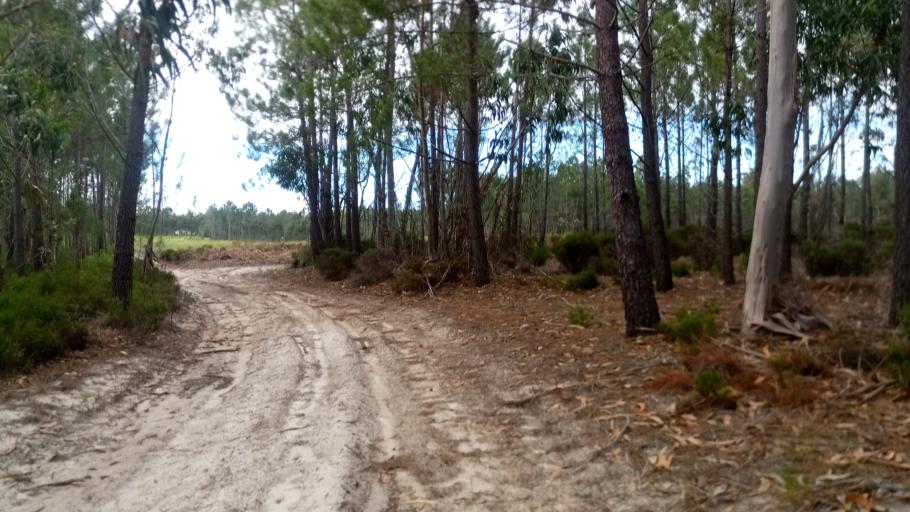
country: PT
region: Leiria
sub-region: Caldas da Rainha
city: Caldas da Rainha
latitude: 39.4488
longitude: -9.1678
